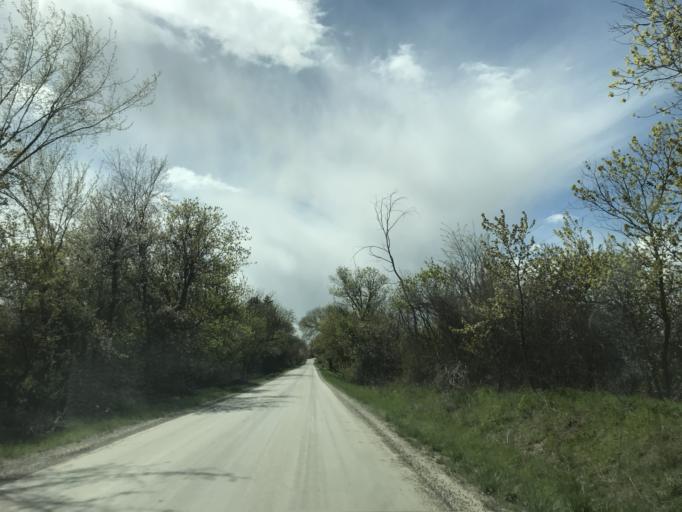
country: US
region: Michigan
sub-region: Oakland County
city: South Lyon
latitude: 42.3882
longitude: -83.6361
